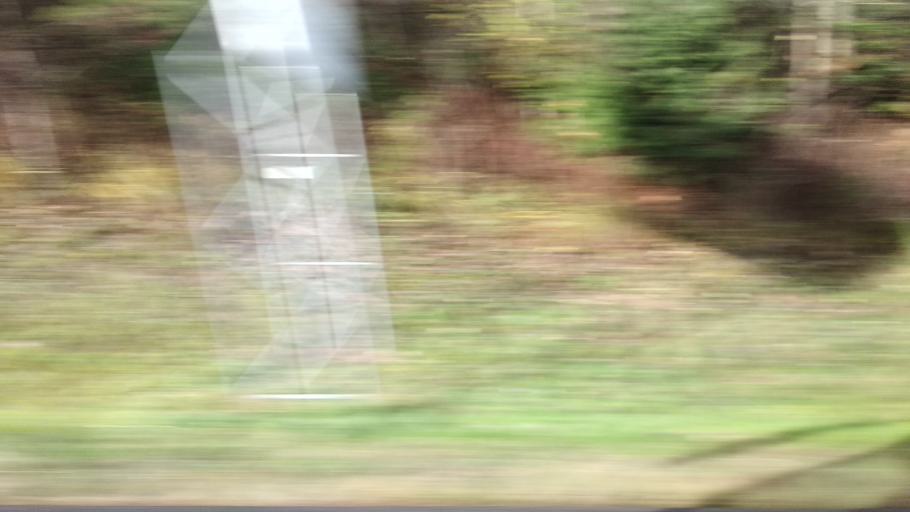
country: DE
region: Bavaria
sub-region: Swabia
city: Weissensberg
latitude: 47.6152
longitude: 9.7352
